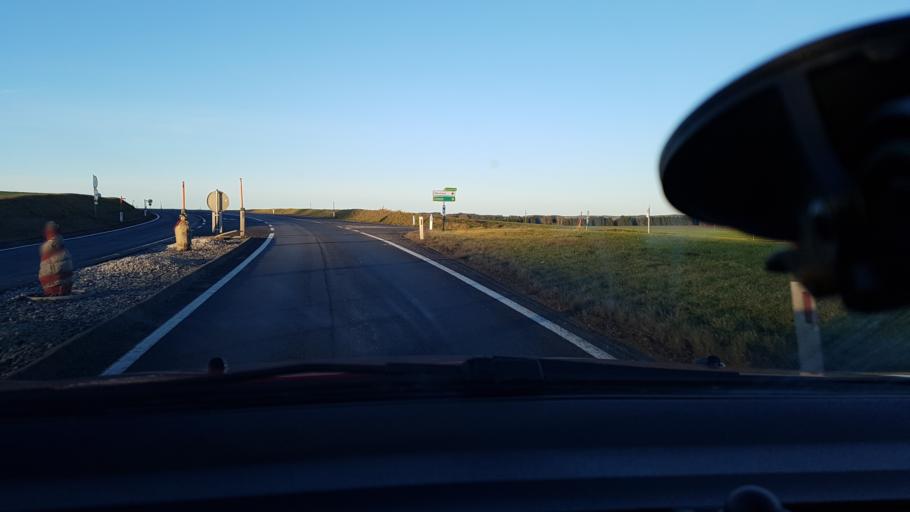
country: AT
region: Salzburg
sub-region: Politischer Bezirk Salzburg-Umgebung
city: Dorfbeuern
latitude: 48.0358
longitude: 12.9838
